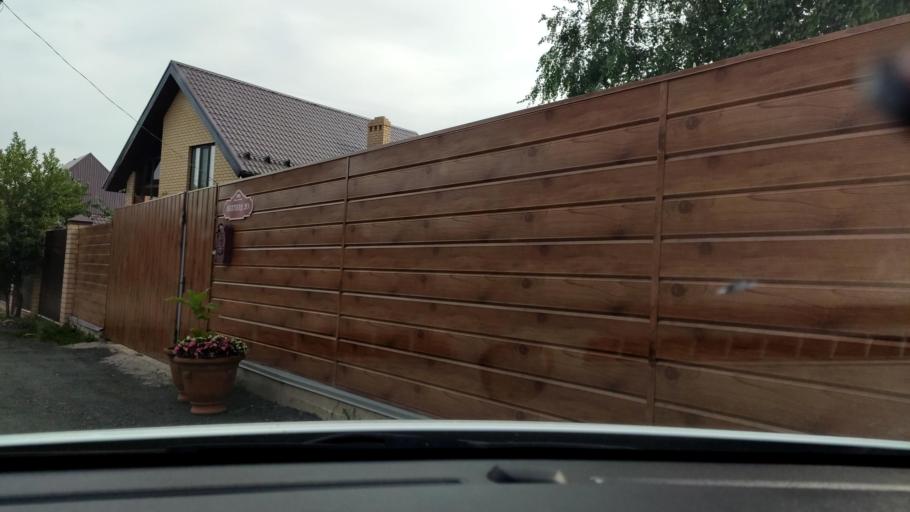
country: RU
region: Tatarstan
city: Stolbishchi
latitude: 55.7590
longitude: 49.2967
